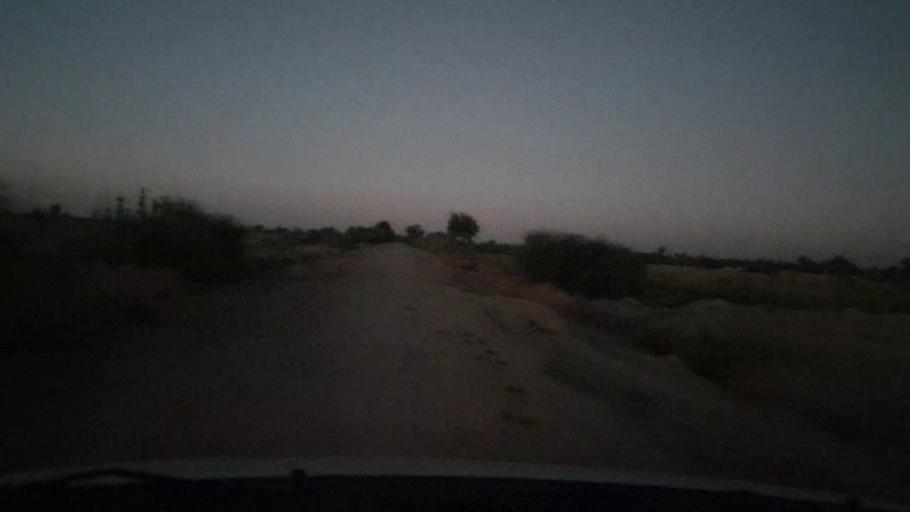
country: PK
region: Sindh
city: Phulji
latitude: 26.9036
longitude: 67.4771
